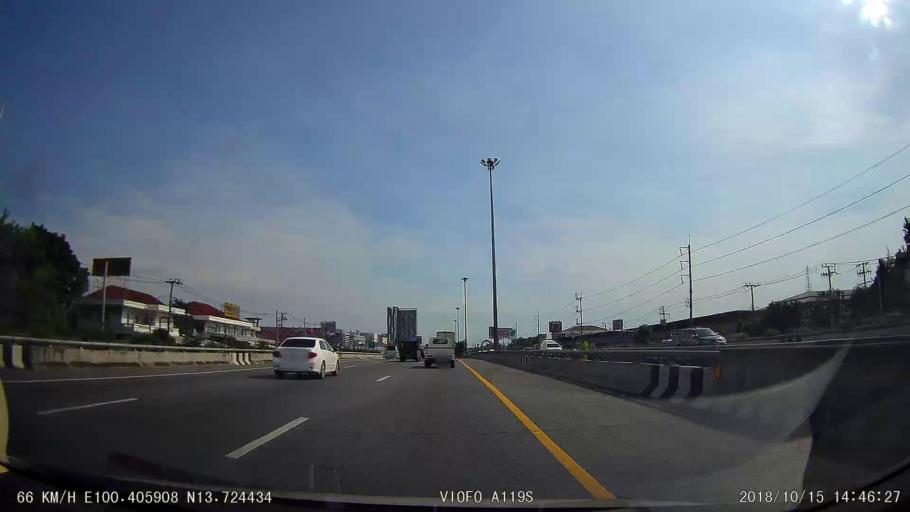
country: TH
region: Bangkok
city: Bang Khae
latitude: 13.7241
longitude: 100.4059
